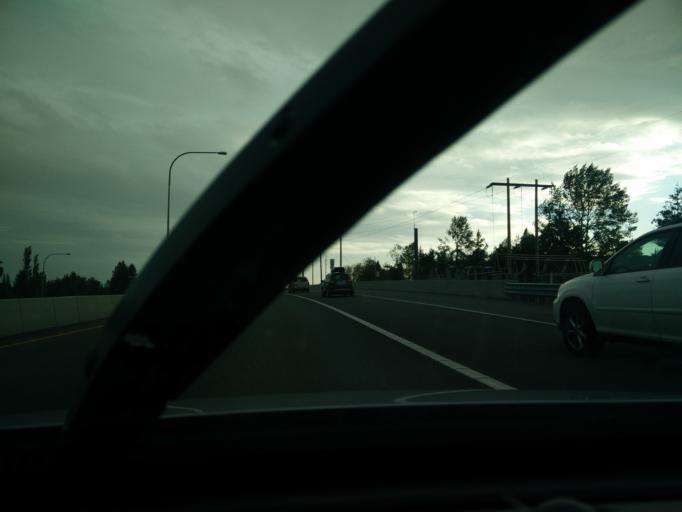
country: US
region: Washington
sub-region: Snohomish County
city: Alderwood Manor
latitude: 47.8299
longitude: -122.2652
